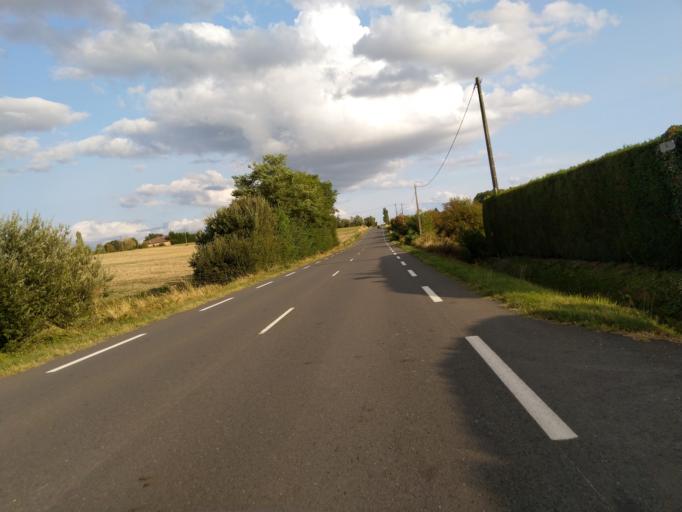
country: FR
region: Midi-Pyrenees
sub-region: Departement du Tarn
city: Frejairolles
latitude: 43.8962
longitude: 2.2137
